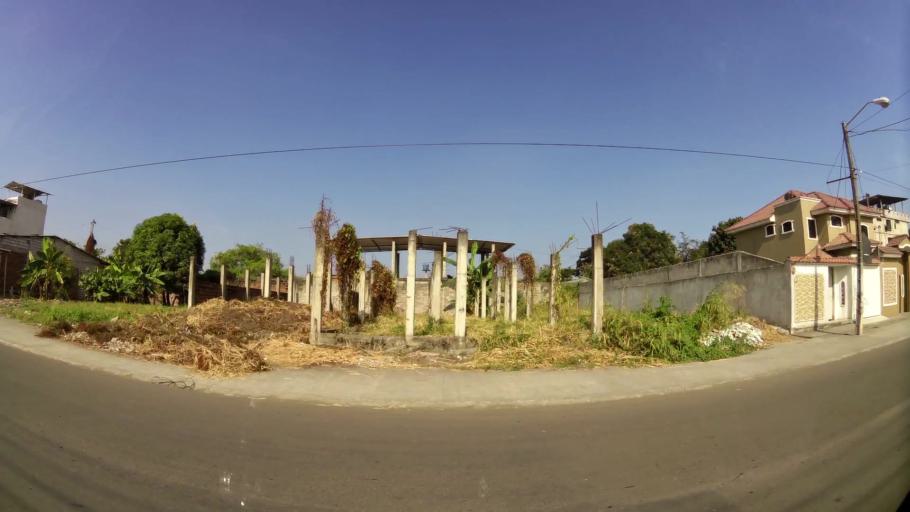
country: EC
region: Guayas
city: Eloy Alfaro
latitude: -2.1906
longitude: -79.8198
